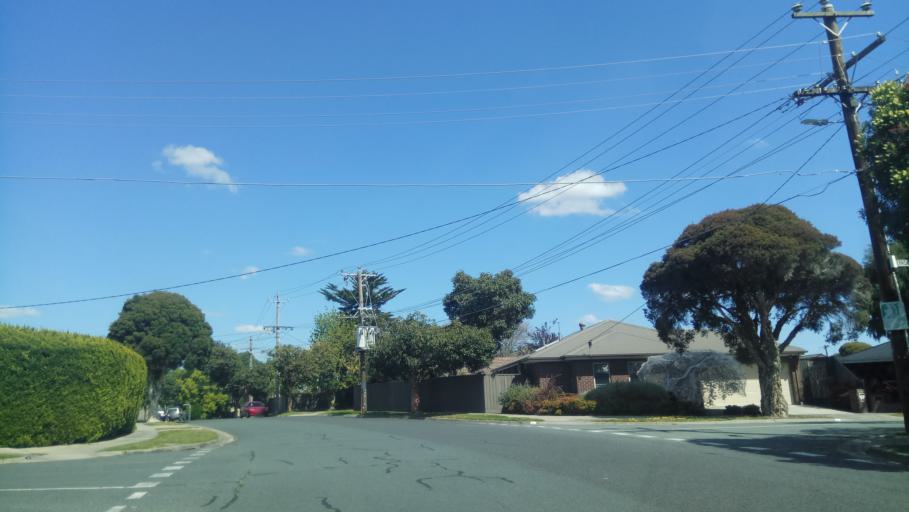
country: AU
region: Victoria
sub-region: Kingston
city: Dingley Village
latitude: -37.9789
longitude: 145.1195
